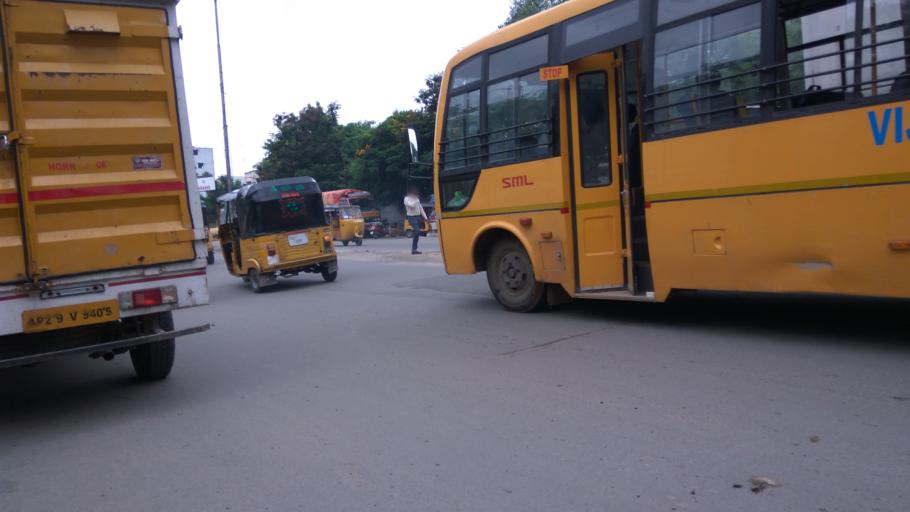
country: IN
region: Telangana
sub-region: Hyderabad
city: Malkajgiri
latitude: 17.4319
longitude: 78.5057
